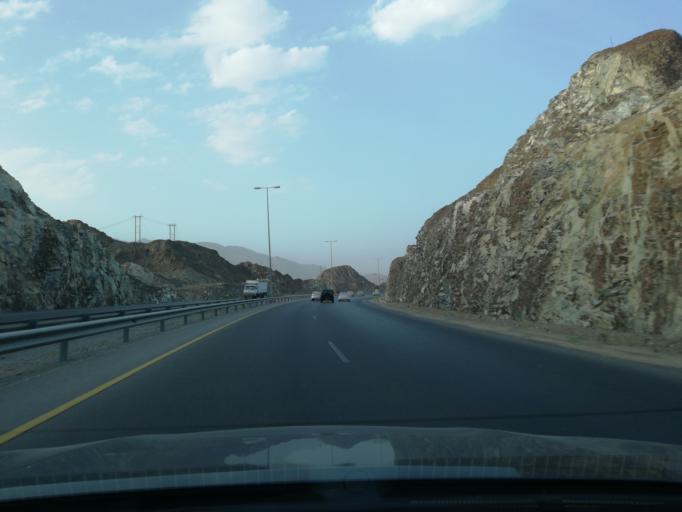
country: OM
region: Muhafazat ad Dakhiliyah
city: Sufalat Sama'il
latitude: 23.3613
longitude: 58.0323
